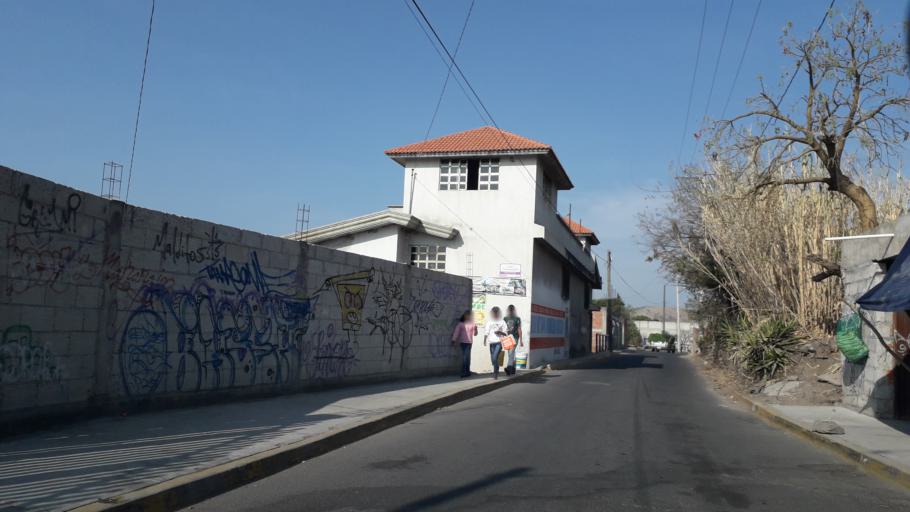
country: MX
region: Puebla
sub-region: Puebla
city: San Andres Azumiatla
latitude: 18.9023
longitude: -98.2567
